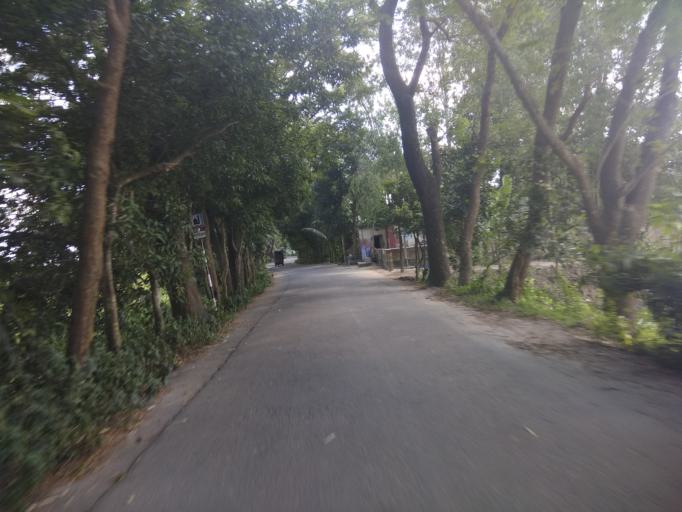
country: BD
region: Dhaka
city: Narayanganj
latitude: 23.4650
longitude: 90.4718
